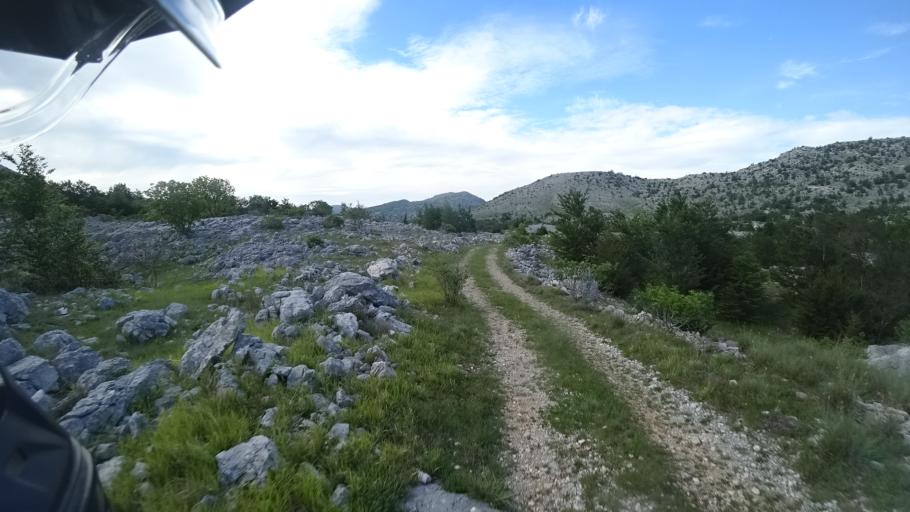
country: HR
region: Splitsko-Dalmatinska
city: Hrvace
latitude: 43.8066
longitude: 16.4338
